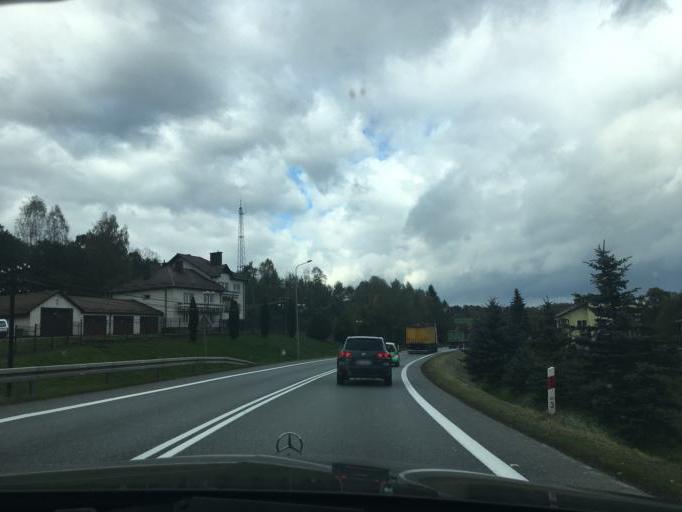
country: PL
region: Subcarpathian Voivodeship
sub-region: Powiat strzyzowski
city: Niebylec
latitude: 49.8637
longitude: 21.9024
